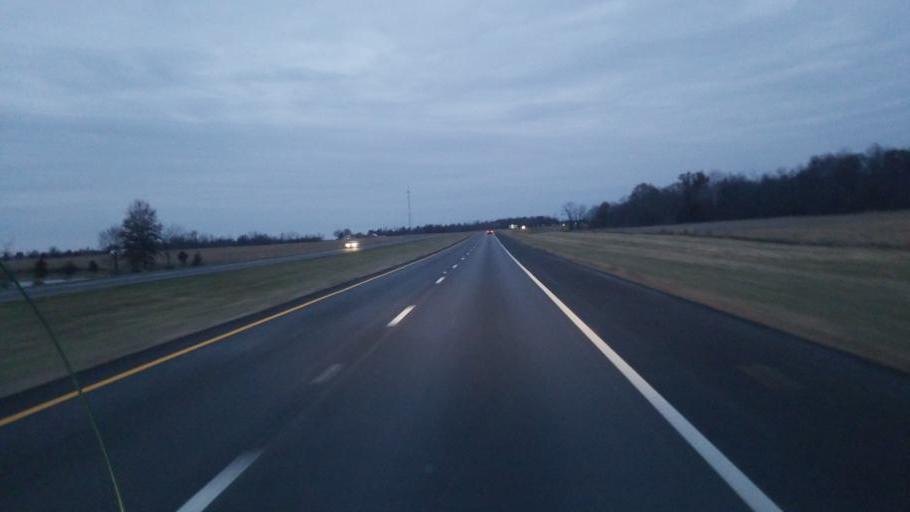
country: US
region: Ohio
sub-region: Hardin County
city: Forest
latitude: 40.8250
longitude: -83.4631
